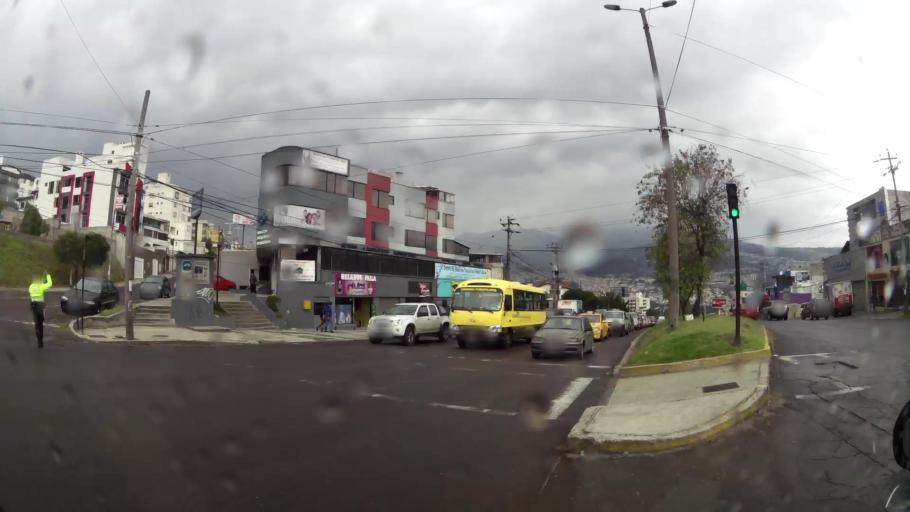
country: EC
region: Pichincha
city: Quito
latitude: -0.0935
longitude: -78.4799
